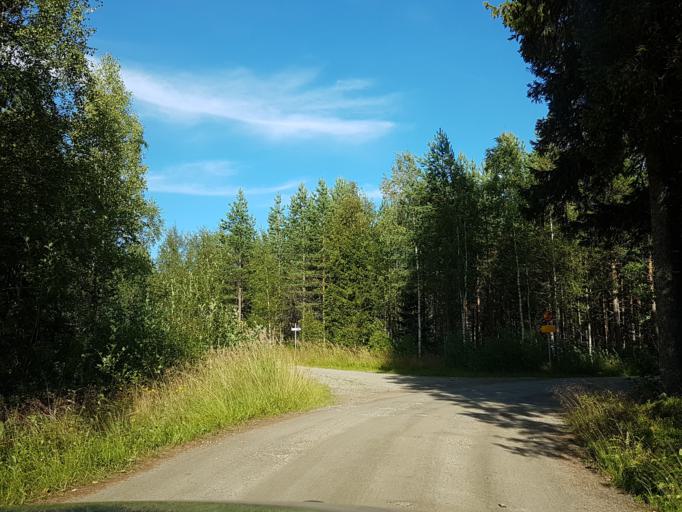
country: SE
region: Vaesterbotten
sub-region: Robertsfors Kommun
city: Robertsfors
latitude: 64.0492
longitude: 20.8858
